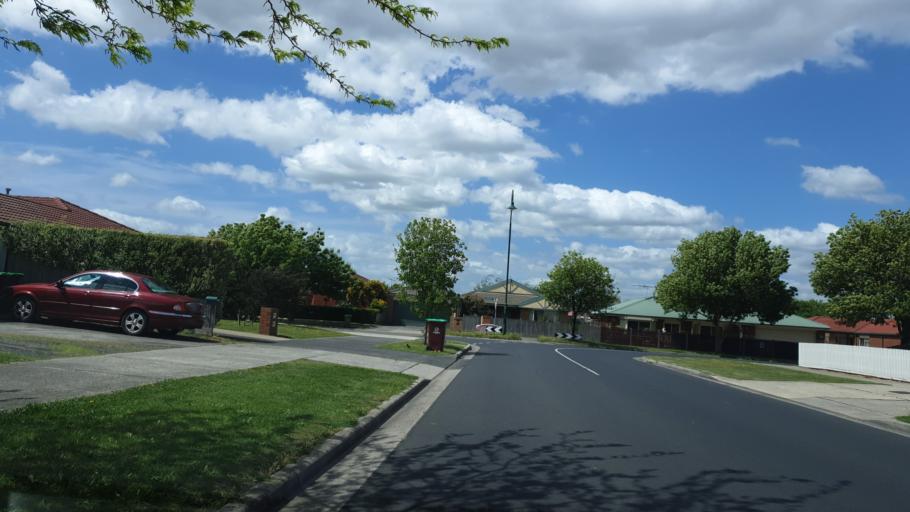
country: AU
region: Victoria
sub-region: Casey
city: Cranbourne
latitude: -38.0970
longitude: 145.2951
